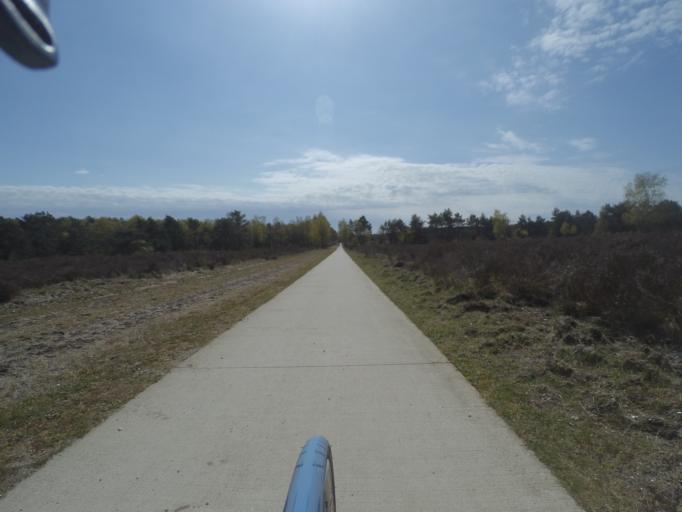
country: NL
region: Gelderland
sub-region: Gemeente Epe
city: Emst
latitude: 52.3259
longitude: 5.8860
